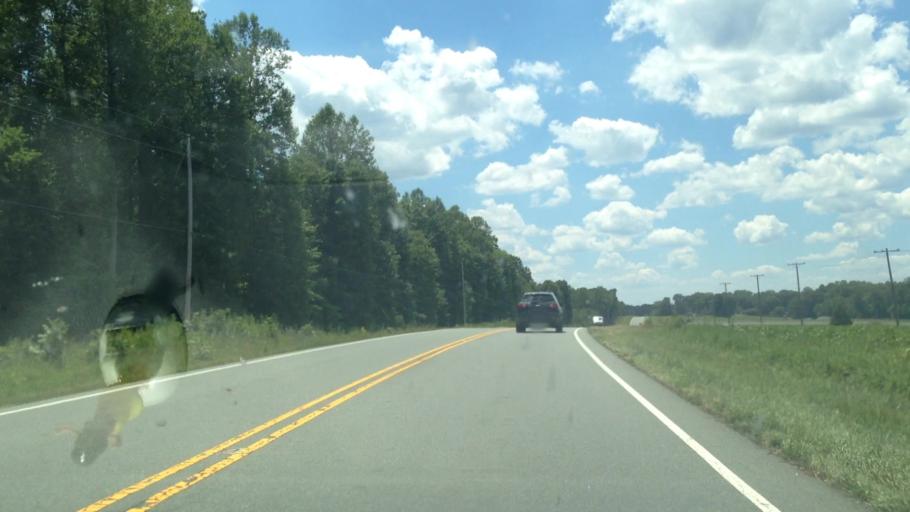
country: US
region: North Carolina
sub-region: Forsyth County
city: Walkertown
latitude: 36.1968
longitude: -80.0945
